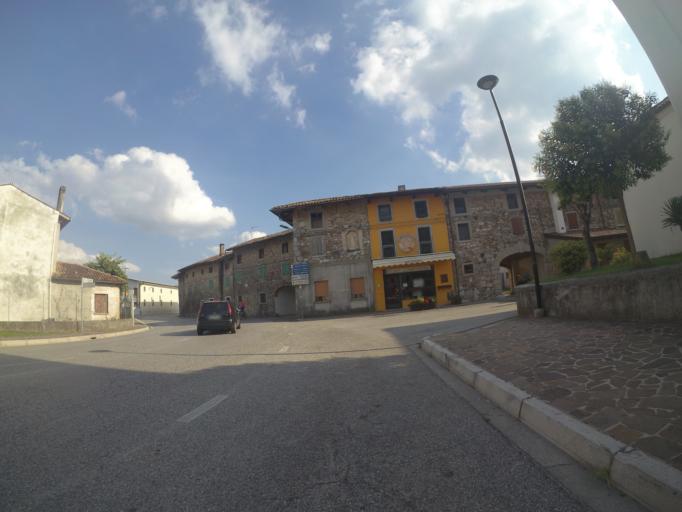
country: IT
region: Friuli Venezia Giulia
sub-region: Provincia di Udine
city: San Vito di Fagagna
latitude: 46.0673
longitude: 13.0822
